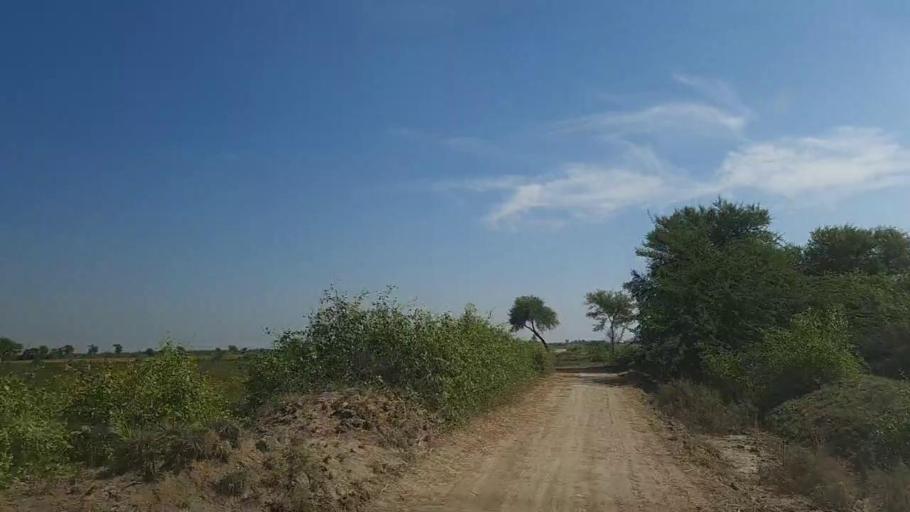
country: PK
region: Sindh
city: Mirpur Batoro
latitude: 24.7562
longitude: 68.3016
